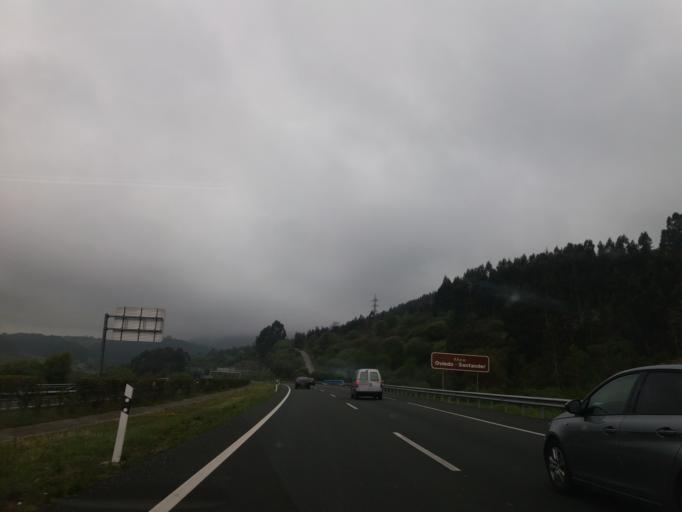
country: ES
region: Cantabria
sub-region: Provincia de Cantabria
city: San Vicente de la Barquera
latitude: 43.3593
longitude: -4.3946
